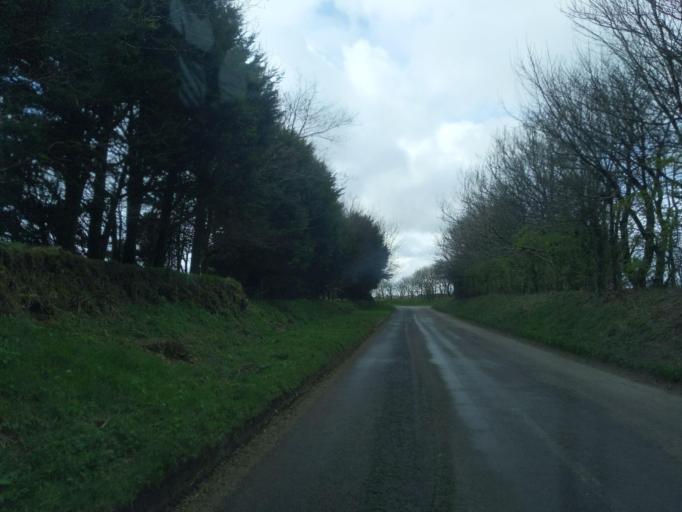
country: GB
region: England
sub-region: Cornwall
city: Camelford
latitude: 50.6248
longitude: -4.5783
